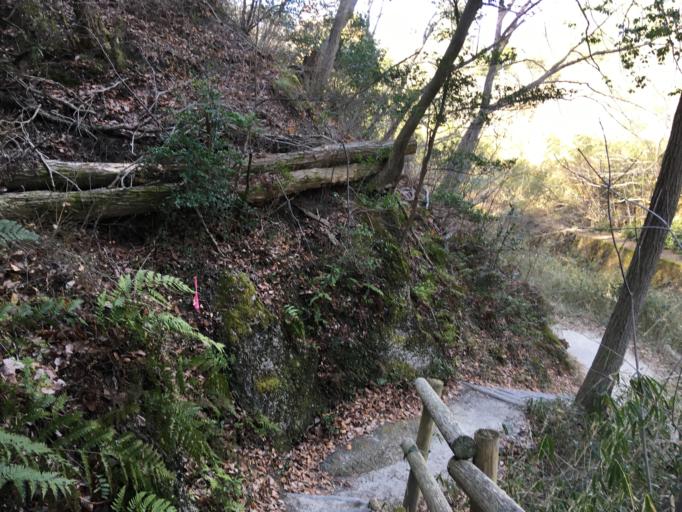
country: JP
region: Osaka
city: Neyagawa
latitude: 34.7579
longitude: 135.6888
